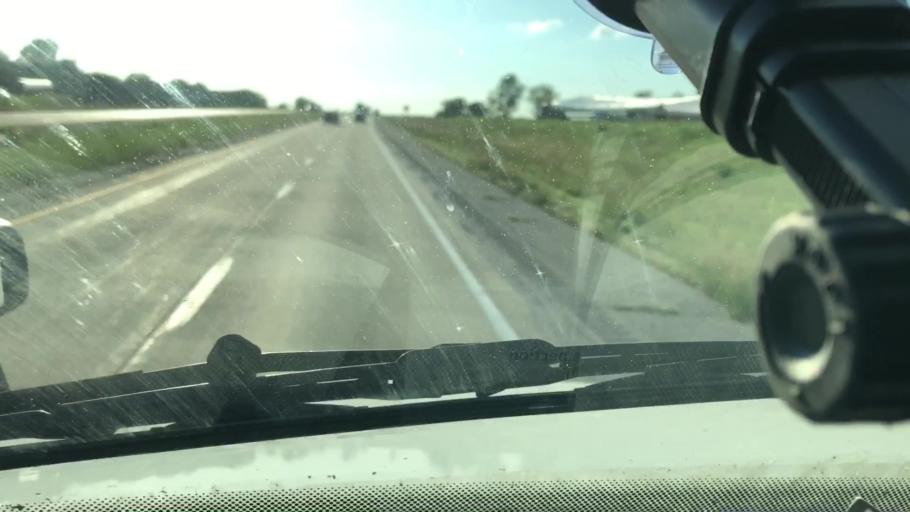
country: US
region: Iowa
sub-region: Pottawattamie County
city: Avoca
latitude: 41.4990
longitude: -95.4915
